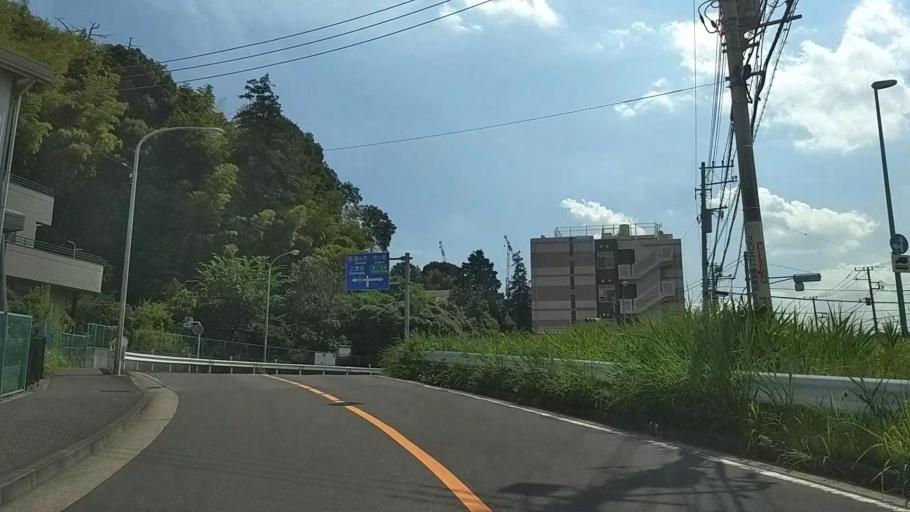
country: JP
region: Kanagawa
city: Yokohama
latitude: 35.5089
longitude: 139.5645
